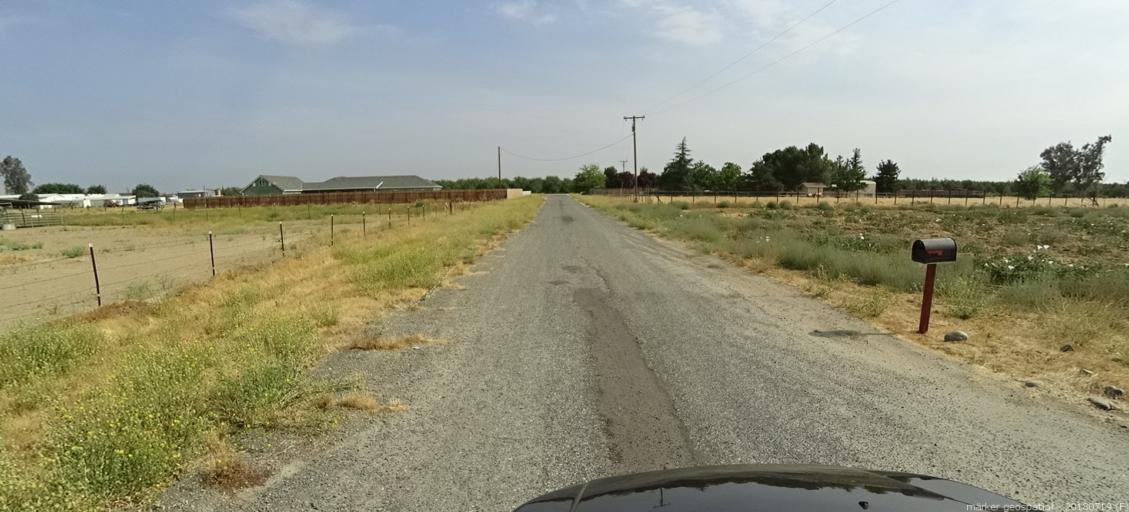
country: US
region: California
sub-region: Madera County
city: Fairmead
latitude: 37.1037
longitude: -120.2089
